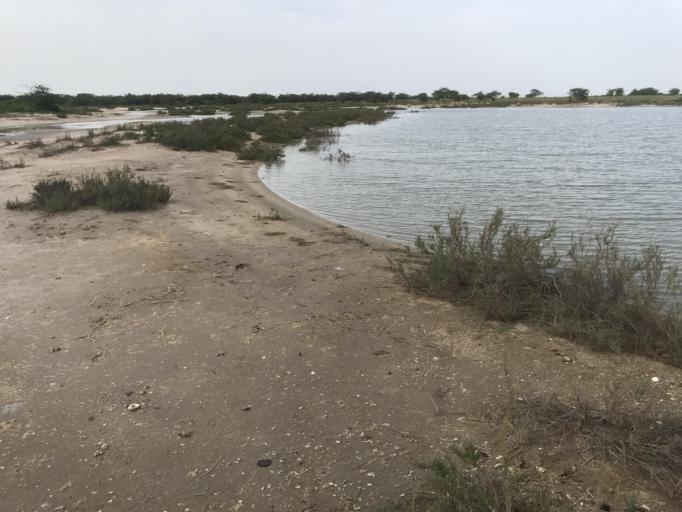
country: SN
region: Saint-Louis
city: Saint-Louis
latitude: 15.9288
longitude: -16.4637
